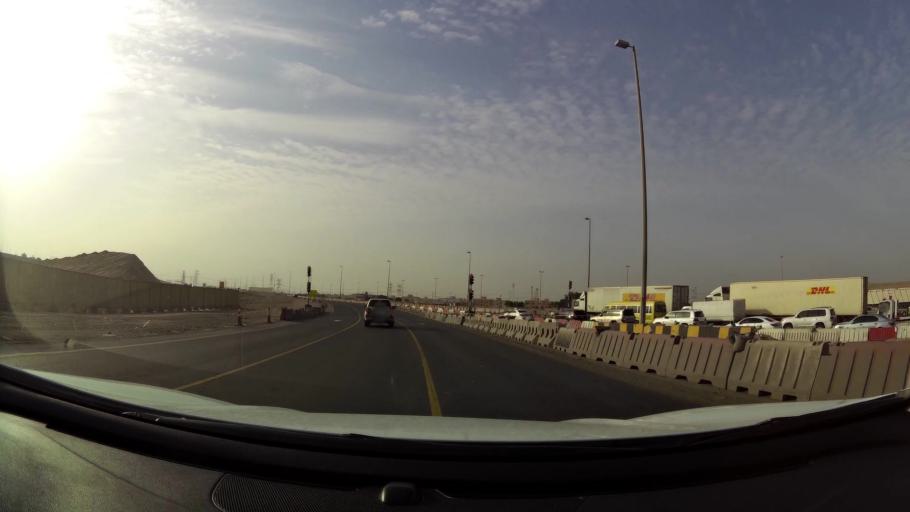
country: AE
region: Abu Dhabi
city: Abu Dhabi
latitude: 24.2917
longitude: 54.5593
